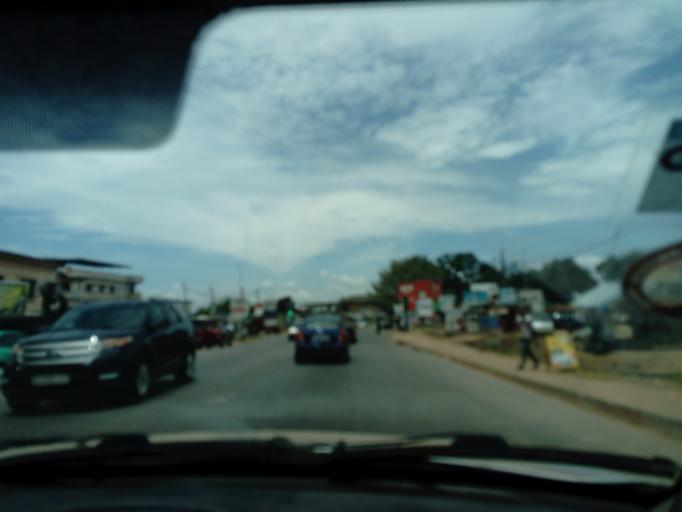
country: GH
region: Central
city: Cape Coast
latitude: 5.1278
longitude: -1.2734
